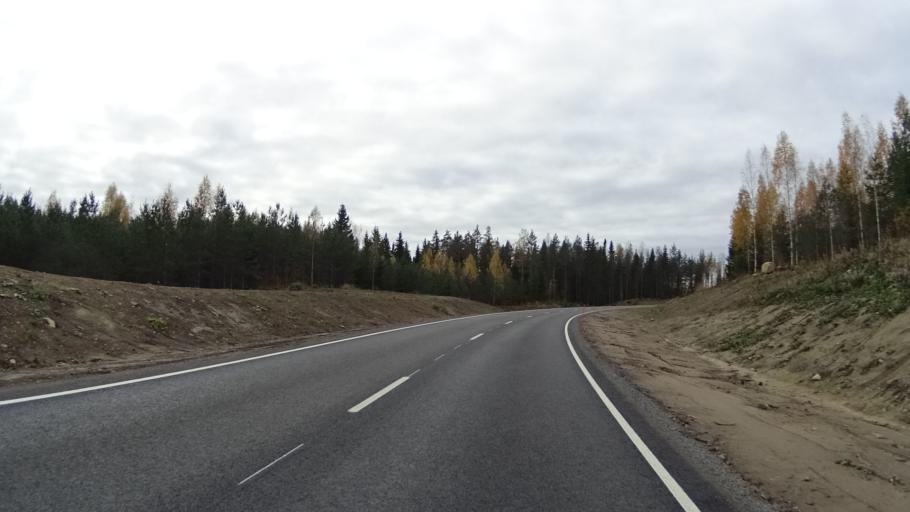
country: FI
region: South Karelia
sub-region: Lappeenranta
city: Taipalsaari
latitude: 61.0273
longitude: 28.0303
